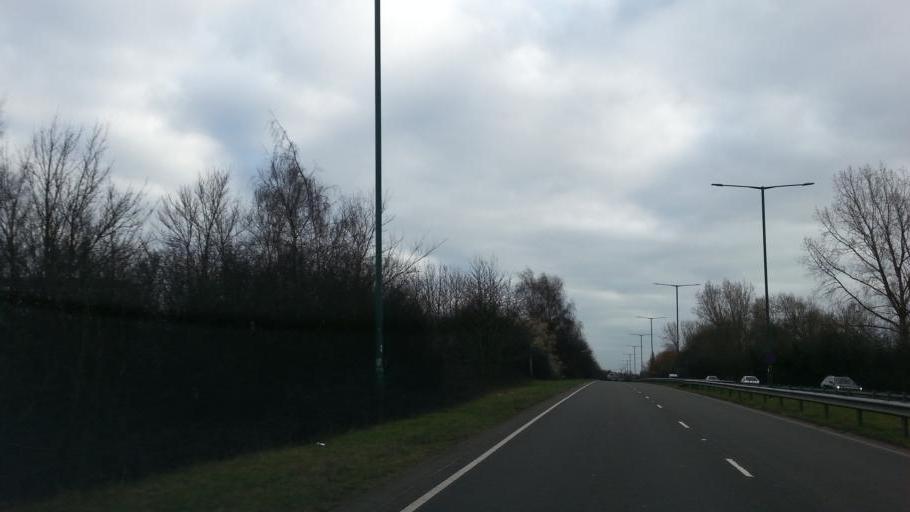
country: GB
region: England
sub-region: Warwickshire
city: Water Orton
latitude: 52.4988
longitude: -1.7386
